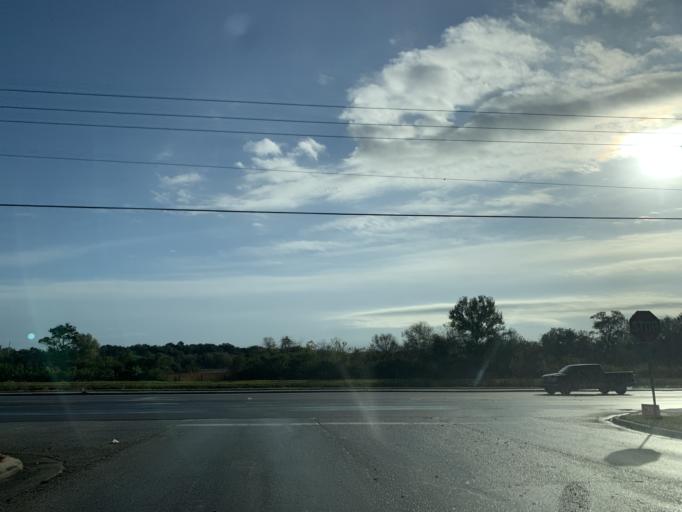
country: US
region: Florida
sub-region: Hillsborough County
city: Mango
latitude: 27.9799
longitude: -82.3190
